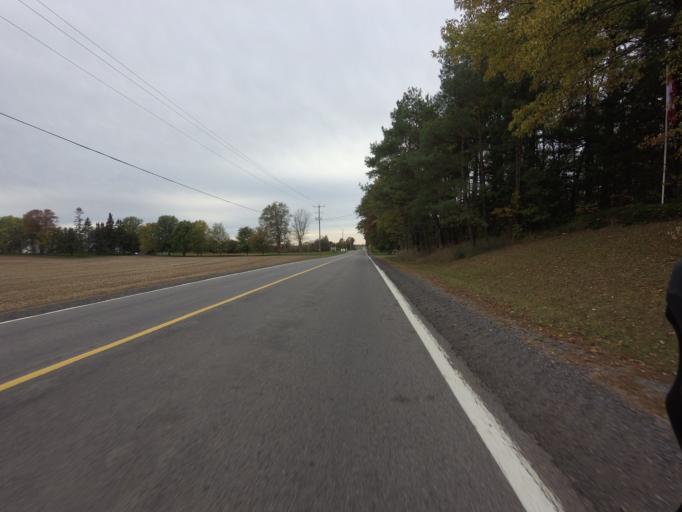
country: CA
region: Ontario
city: Bells Corners
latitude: 45.1130
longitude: -75.7273
